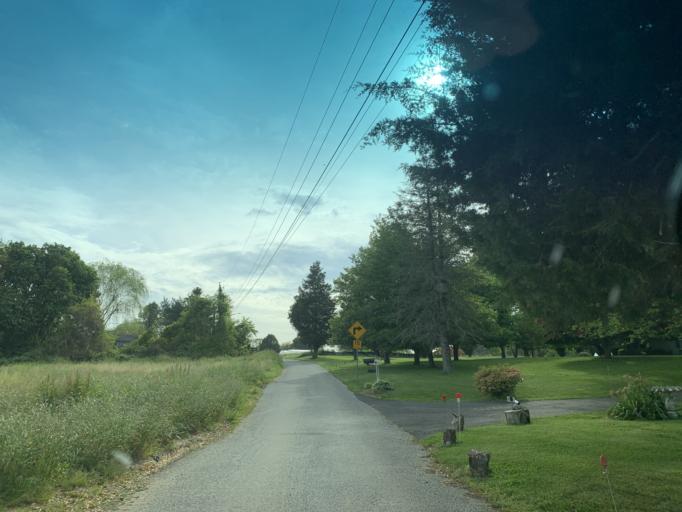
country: US
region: Maryland
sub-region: Baltimore County
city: Perry Hall
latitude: 39.4266
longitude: -76.4846
